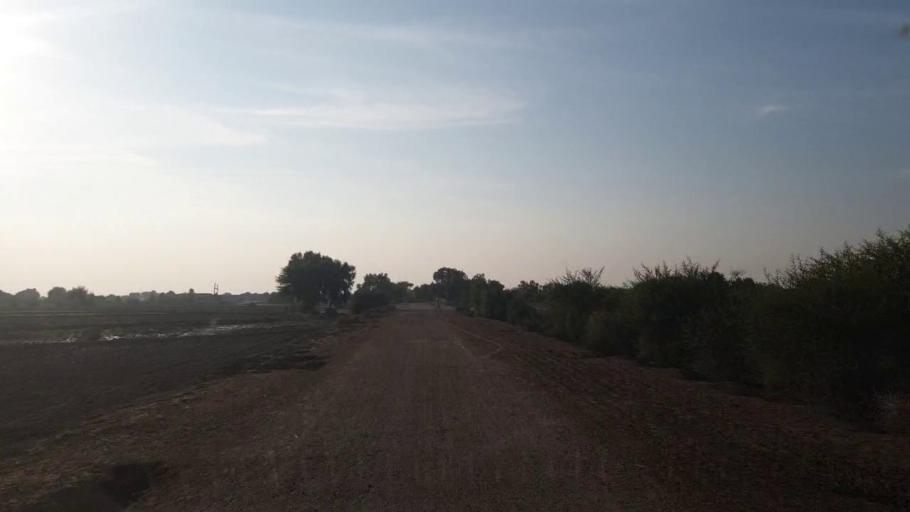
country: PK
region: Sindh
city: Sann
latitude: 25.9457
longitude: 68.1822
